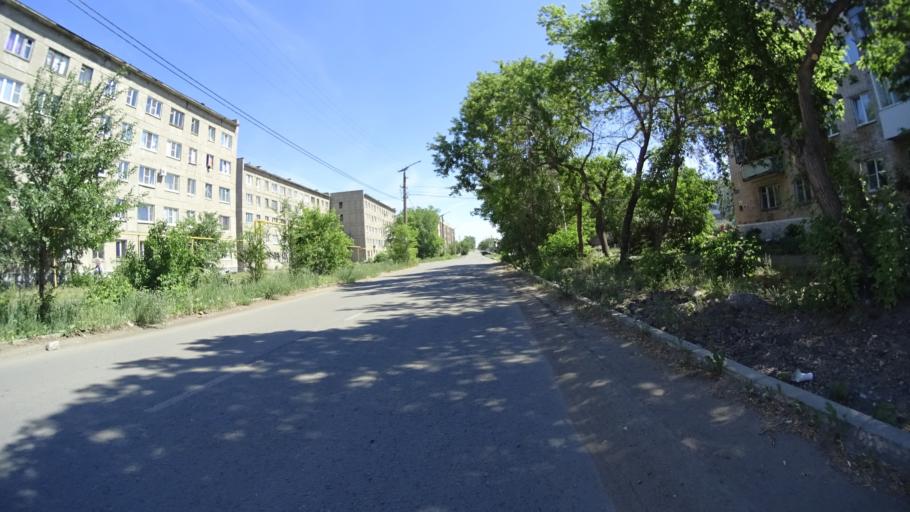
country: RU
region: Chelyabinsk
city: Troitsk
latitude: 54.0924
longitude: 61.5495
